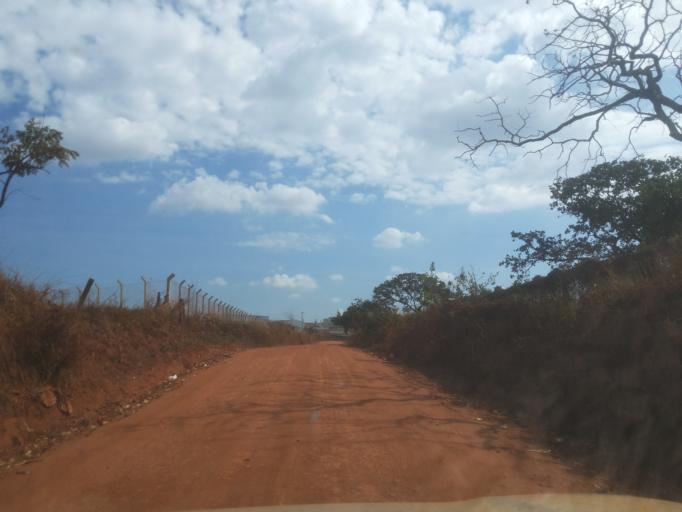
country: BR
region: Minas Gerais
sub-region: Ituiutaba
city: Ituiutaba
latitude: -18.9899
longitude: -49.4276
